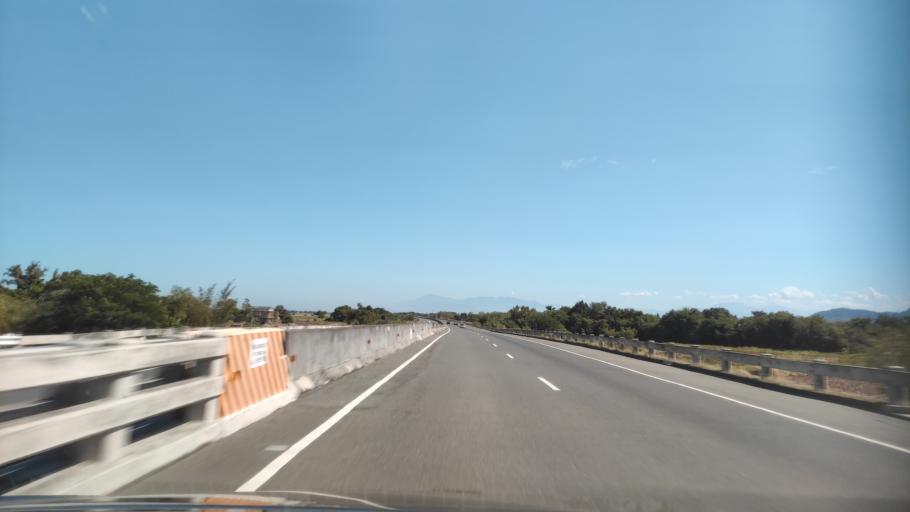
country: PH
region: Central Luzon
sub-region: Province of Nueva Ecija
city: Calancuasan Norte
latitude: 15.7925
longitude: 120.6416
